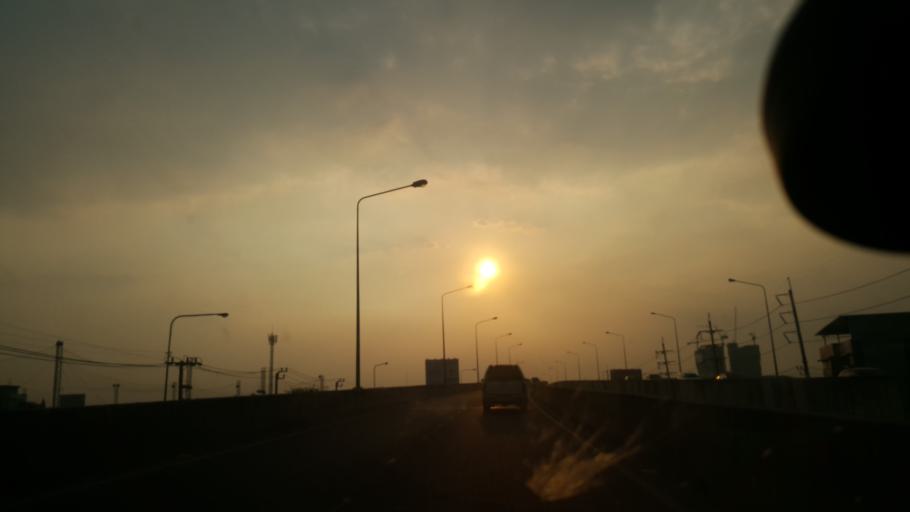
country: TH
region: Bangkok
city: Bang Khae
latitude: 13.6881
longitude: 100.4290
